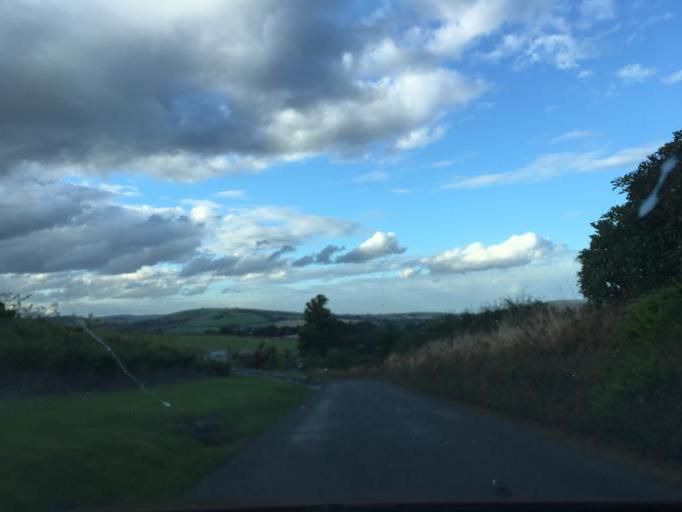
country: IE
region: Leinster
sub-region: Wicklow
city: Wicklow
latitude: 52.9314
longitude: -6.0772
